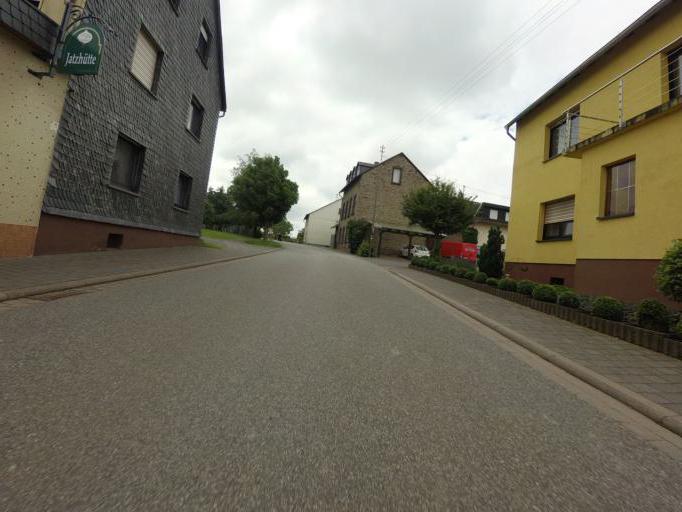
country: DE
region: Rheinland-Pfalz
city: Lahr
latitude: 50.1247
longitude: 7.3665
